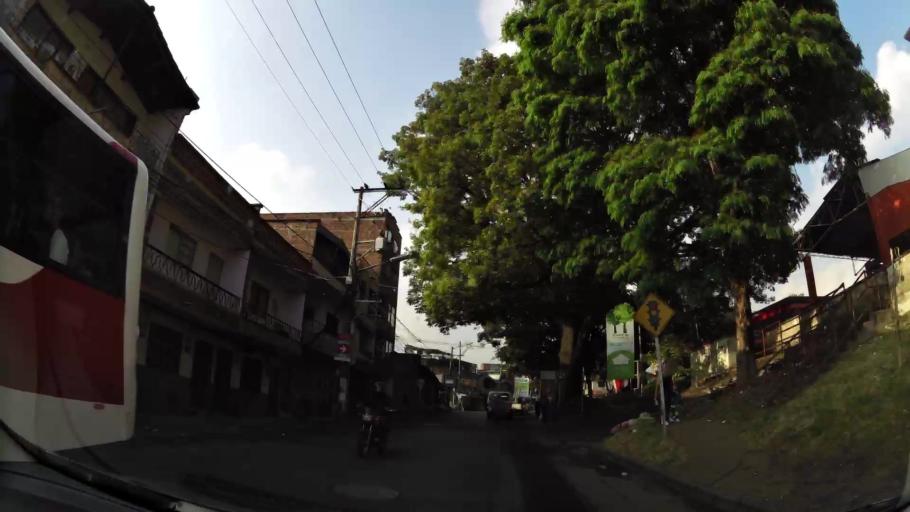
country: CO
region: Antioquia
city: Sabaneta
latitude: 6.1639
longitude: -75.6220
